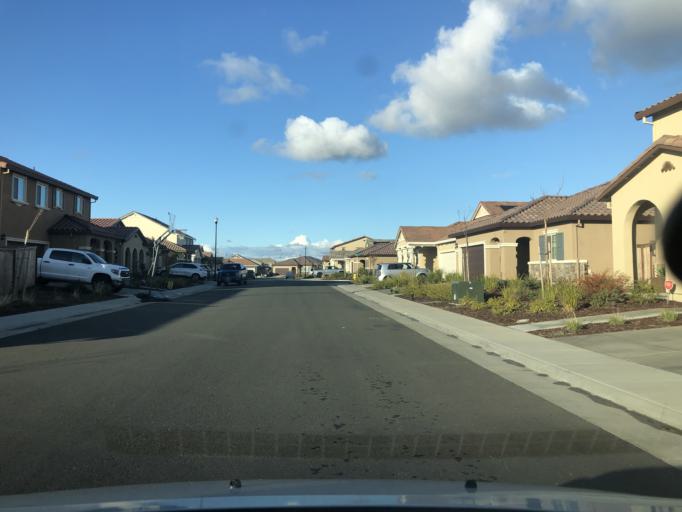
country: US
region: California
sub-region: Sacramento County
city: Antelope
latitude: 38.7734
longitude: -121.3775
